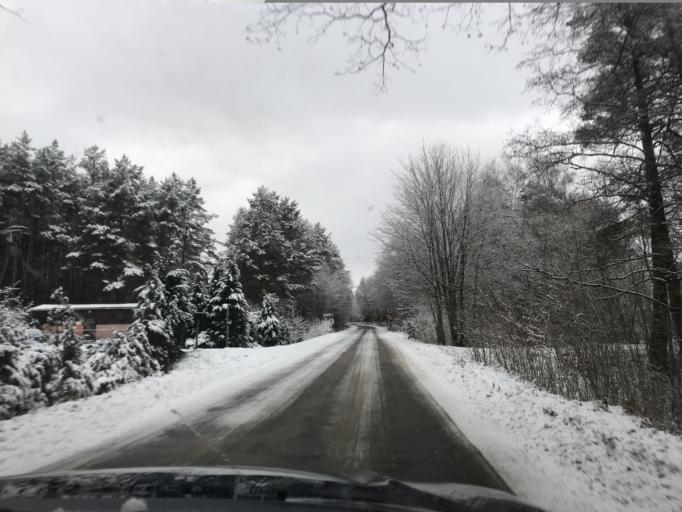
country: PL
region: Pomeranian Voivodeship
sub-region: Powiat bytowski
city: Parchowo
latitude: 54.2530
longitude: 17.5804
